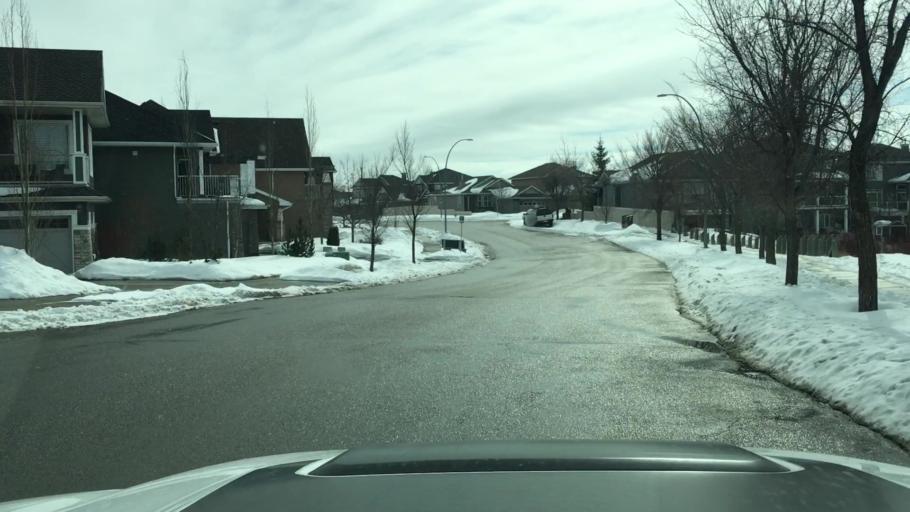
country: CA
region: Alberta
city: Calgary
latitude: 51.1484
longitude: -114.2324
